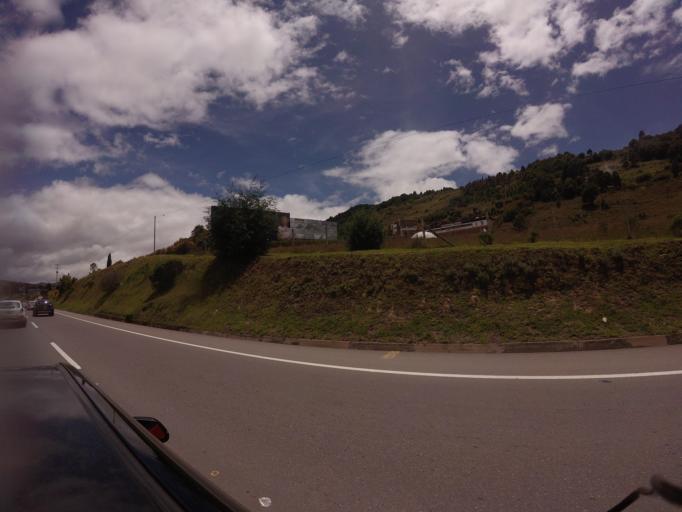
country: CO
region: Boyaca
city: Combita
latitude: 5.6069
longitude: -73.3257
